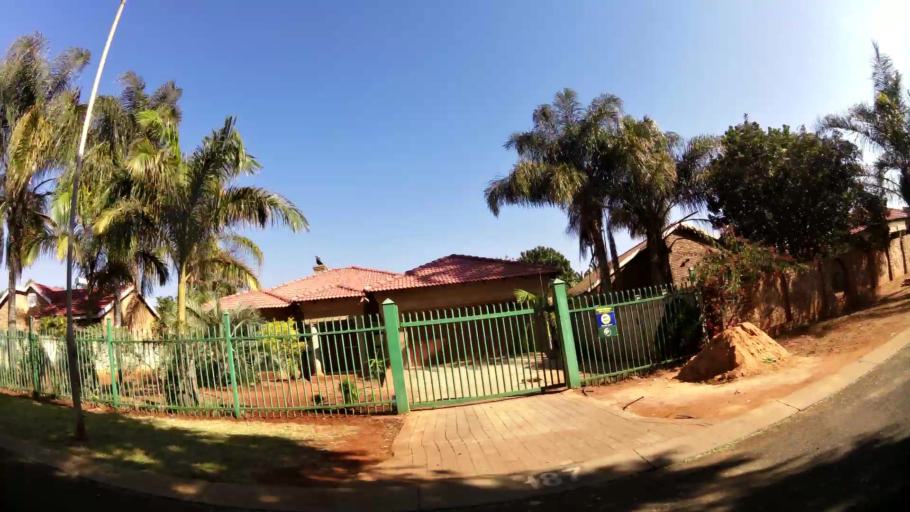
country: ZA
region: North-West
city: Ga-Rankuwa
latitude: -25.6477
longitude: 28.1117
